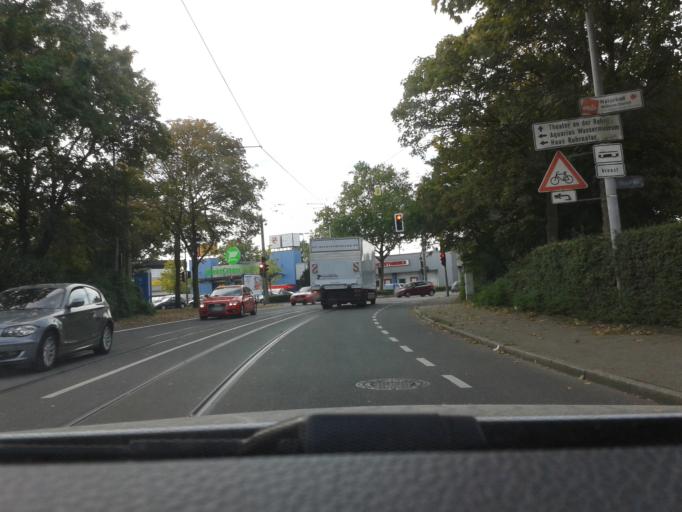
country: DE
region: North Rhine-Westphalia
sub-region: Regierungsbezirk Dusseldorf
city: Muelheim (Ruhr)
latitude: 51.4478
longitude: 6.8481
